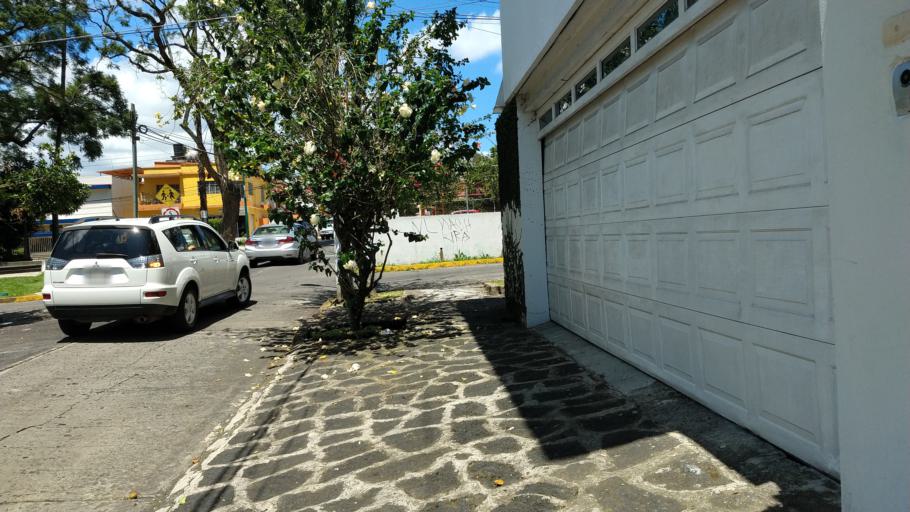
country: MX
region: Veracruz
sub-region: Xalapa
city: Xalapa de Enriquez
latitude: 19.5392
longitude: -96.9288
